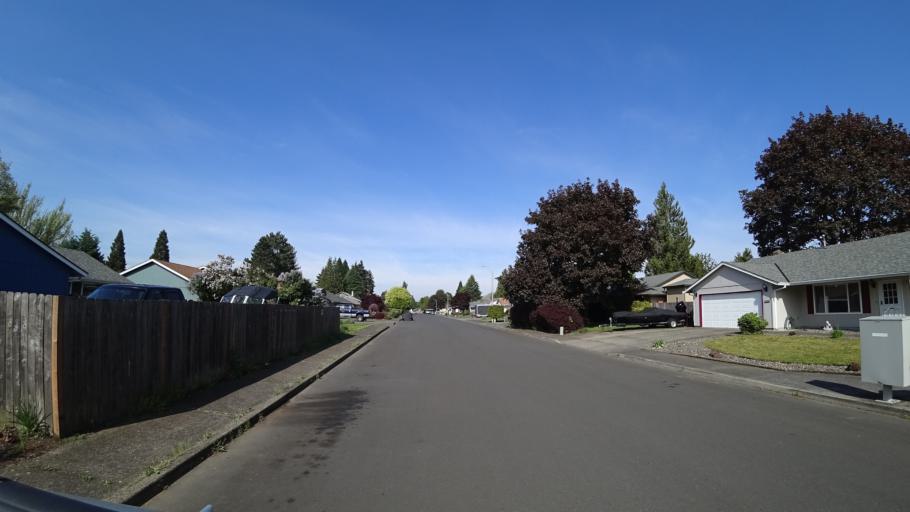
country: US
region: Oregon
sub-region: Washington County
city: Hillsboro
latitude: 45.5225
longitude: -122.9455
